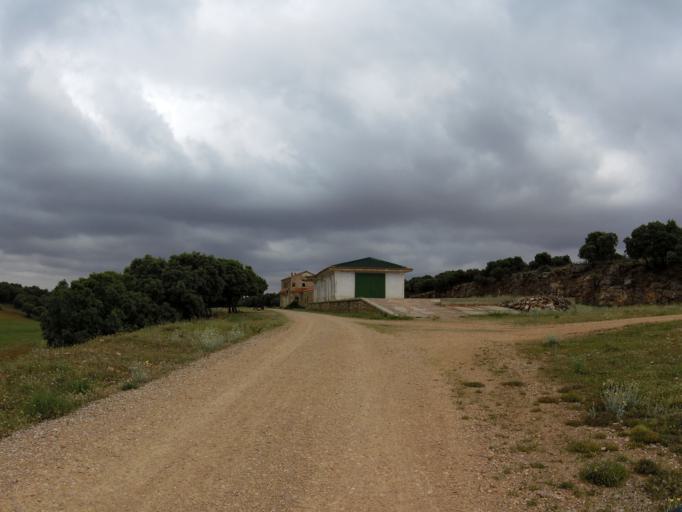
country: ES
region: Castille-La Mancha
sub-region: Provincia de Albacete
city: Robledo
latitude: 38.7428
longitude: -2.4690
